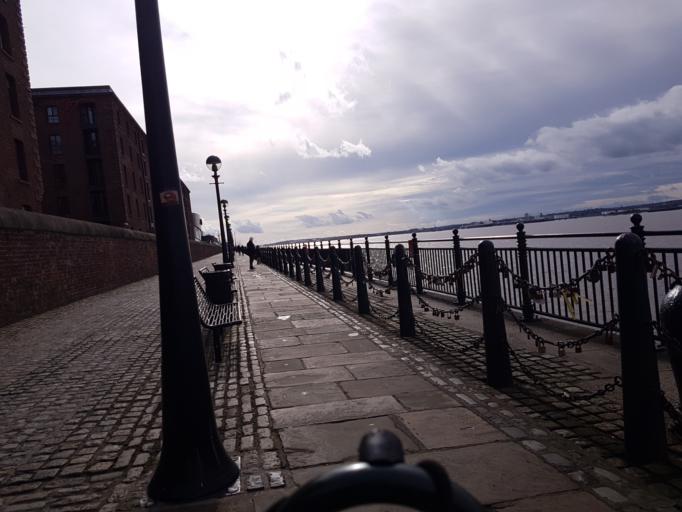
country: GB
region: England
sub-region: Liverpool
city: Liverpool
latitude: 53.4004
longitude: -2.9945
